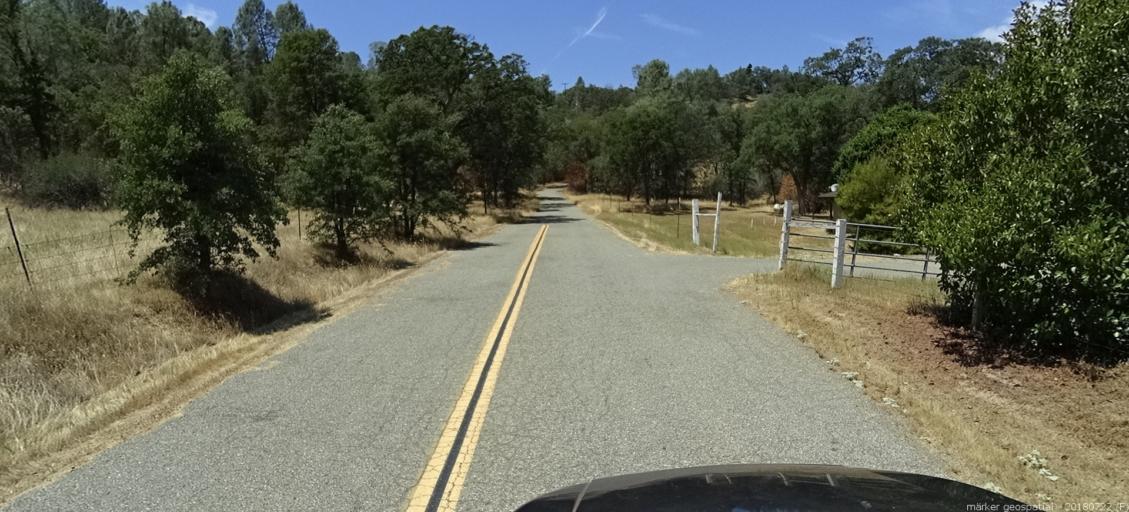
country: US
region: California
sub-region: Madera County
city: Coarsegold
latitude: 37.2499
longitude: -119.7320
